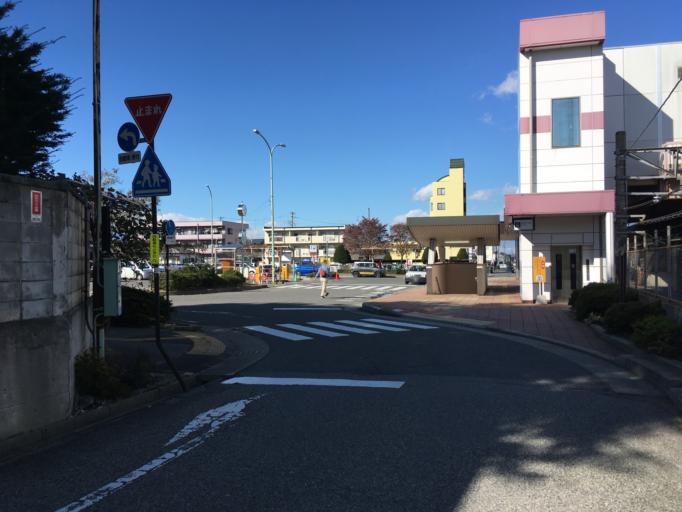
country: JP
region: Nagano
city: Shiojiri
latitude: 36.1141
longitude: 137.9475
